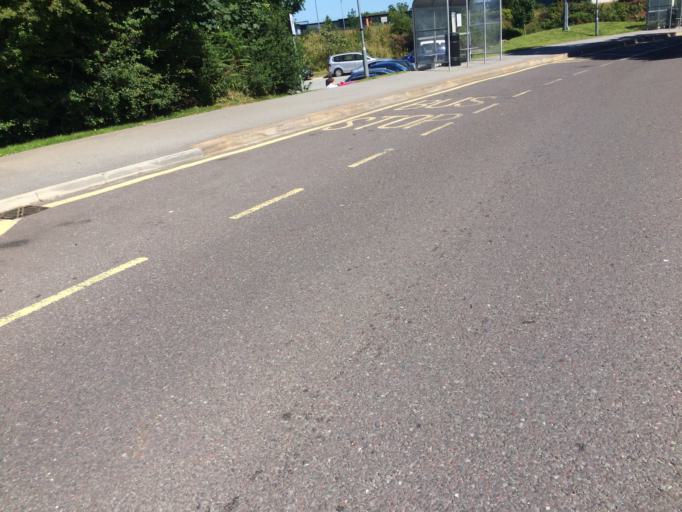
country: GB
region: England
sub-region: Cornwall
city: Penryn
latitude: 50.1724
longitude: -5.1240
